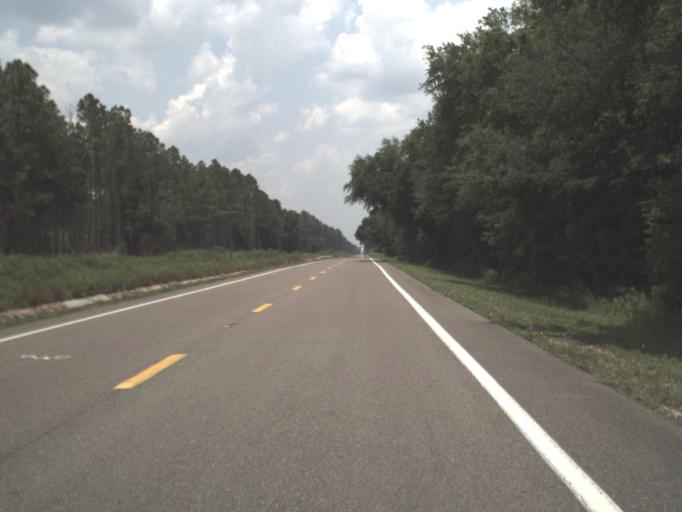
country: US
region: Florida
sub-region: Putnam County
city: Palatka
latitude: 29.4979
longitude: -81.7458
